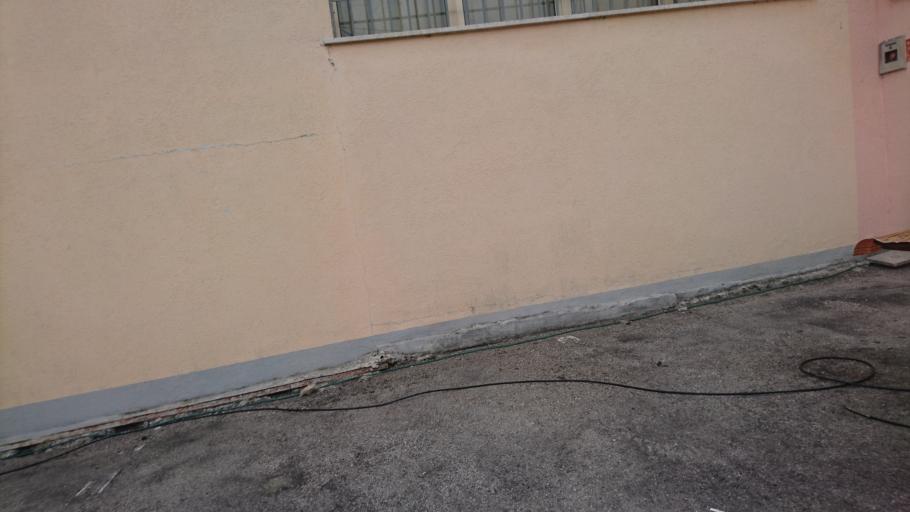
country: IT
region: Veneto
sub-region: Provincia di Padova
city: Gazzo
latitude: 45.5814
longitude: 11.6811
